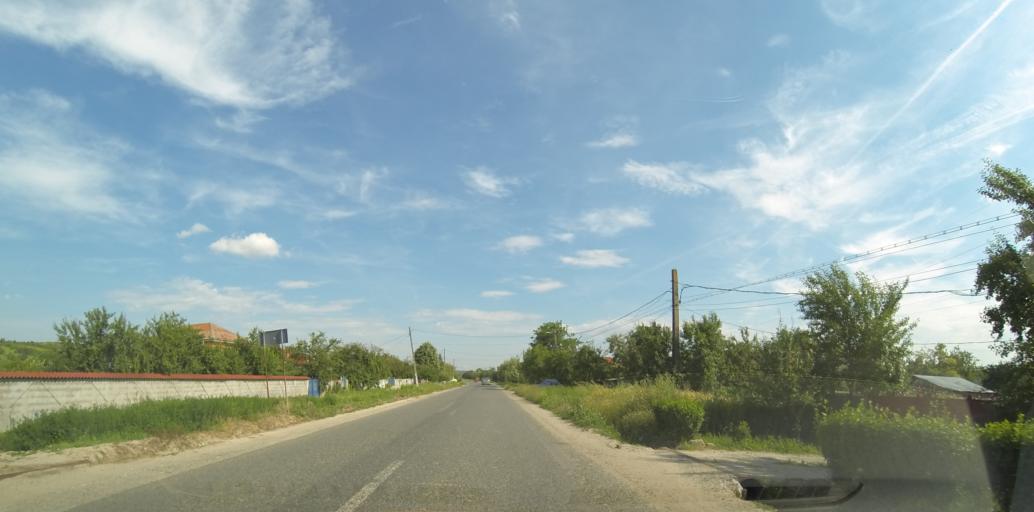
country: RO
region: Dolj
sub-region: Comuna Goesti
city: Goesti
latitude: 44.4695
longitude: 23.7652
